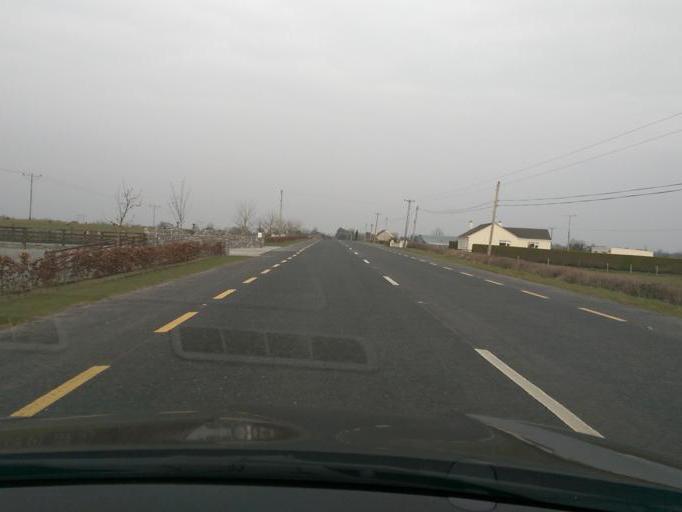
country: IE
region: Leinster
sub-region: An Longfort
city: Lanesborough
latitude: 53.6608
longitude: -8.0783
